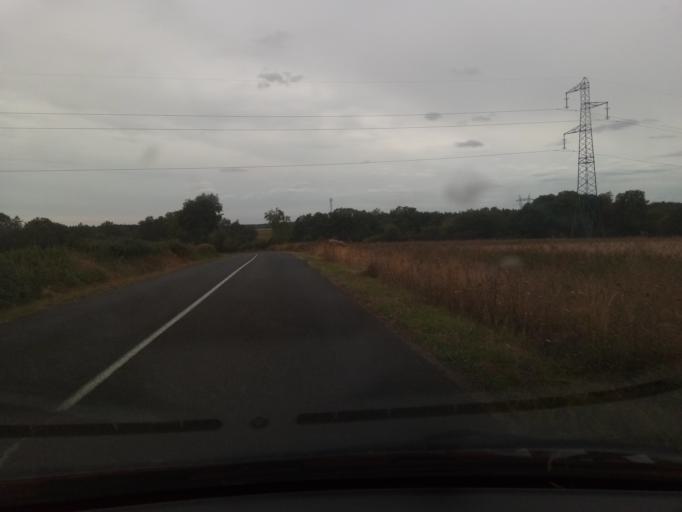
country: FR
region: Centre
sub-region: Departement de l'Indre
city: Tournon-Saint-Martin
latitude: 46.6851
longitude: 0.8715
